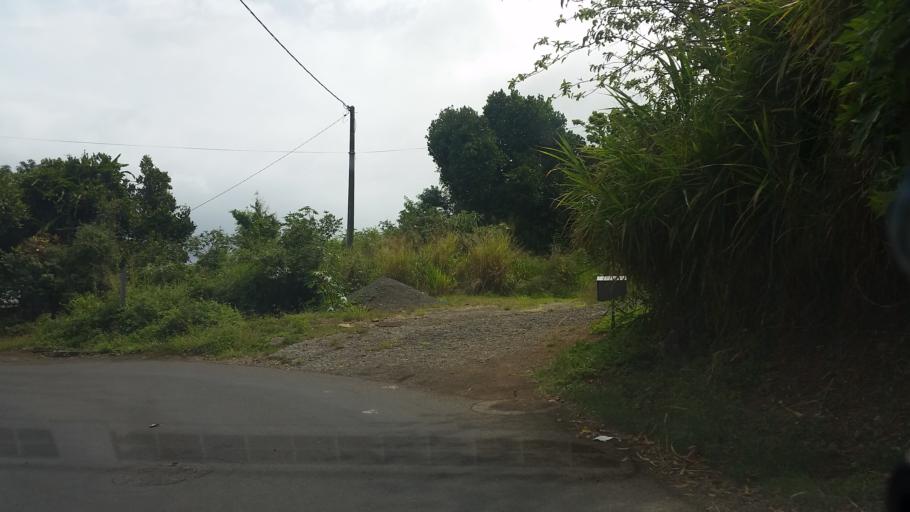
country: RE
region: Reunion
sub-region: Reunion
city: Sainte-Marie
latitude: -20.9173
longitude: 55.5330
